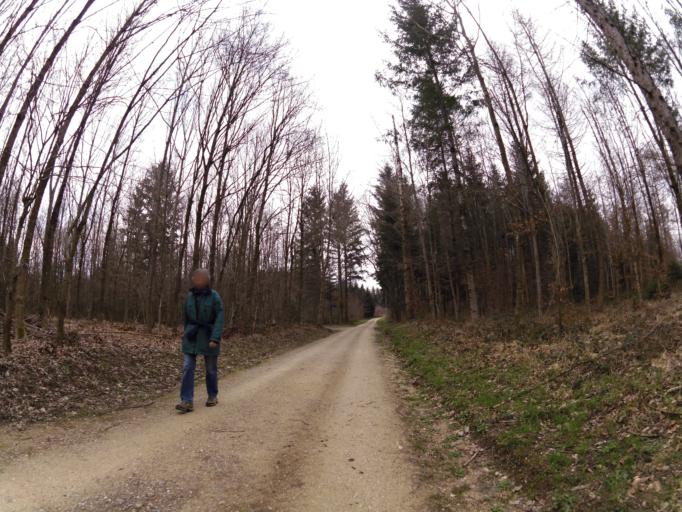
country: CH
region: Aargau
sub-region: Bezirk Aarau
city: Aarau
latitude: 47.3742
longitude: 8.0358
